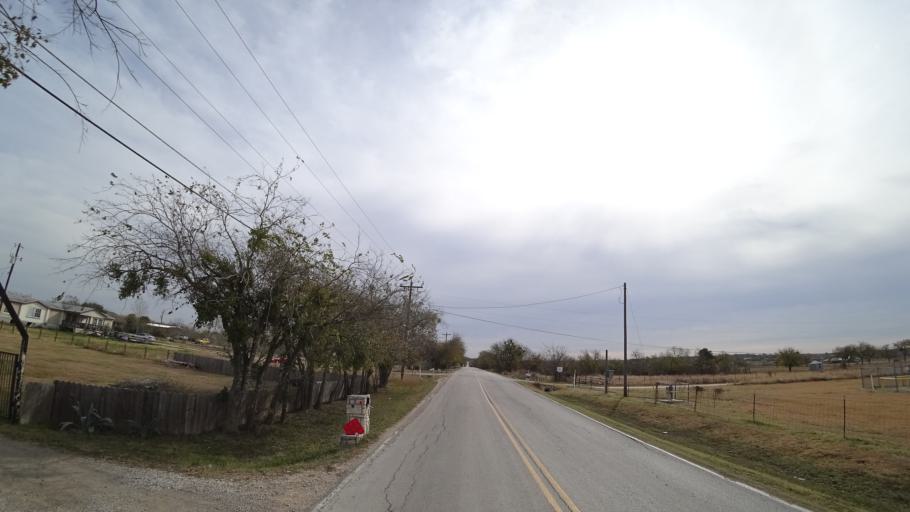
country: US
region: Texas
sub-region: Travis County
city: Garfield
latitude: 30.1216
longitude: -97.5961
